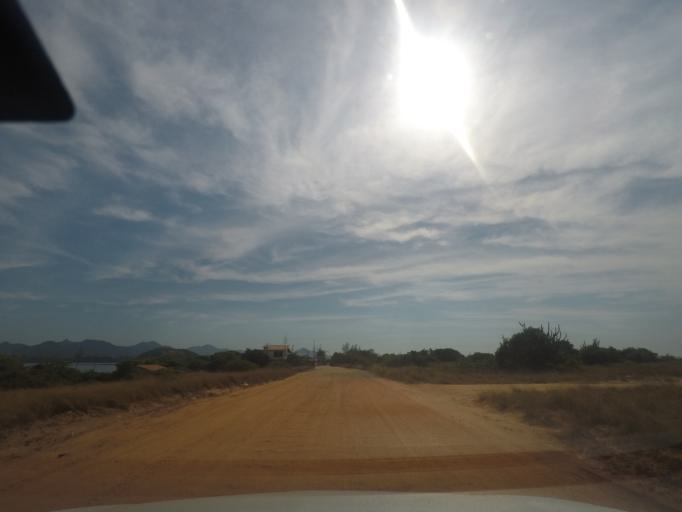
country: BR
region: Rio de Janeiro
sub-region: Marica
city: Marica
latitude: -22.9604
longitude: -42.8399
